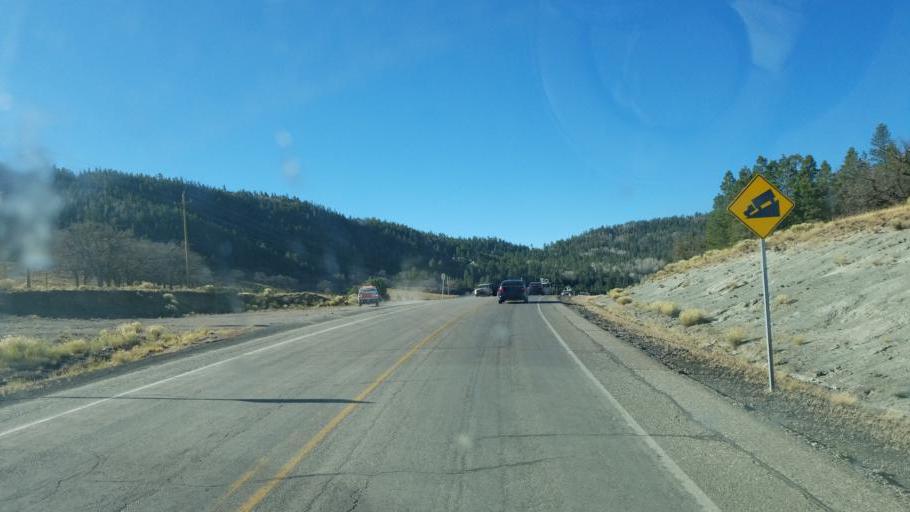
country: US
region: New Mexico
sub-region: McKinley County
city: Navajo
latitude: 36.0902
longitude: -108.8600
